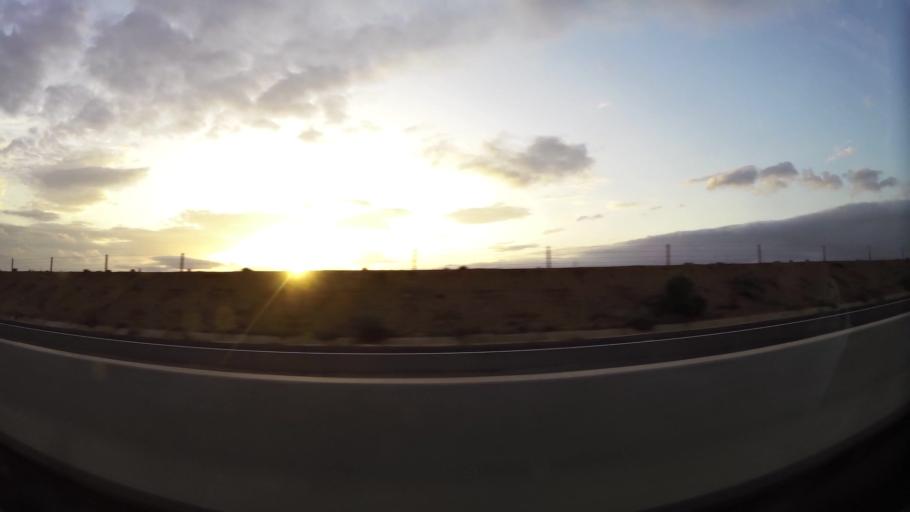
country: MA
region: Oriental
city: Taourirt
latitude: 34.5393
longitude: -2.9126
